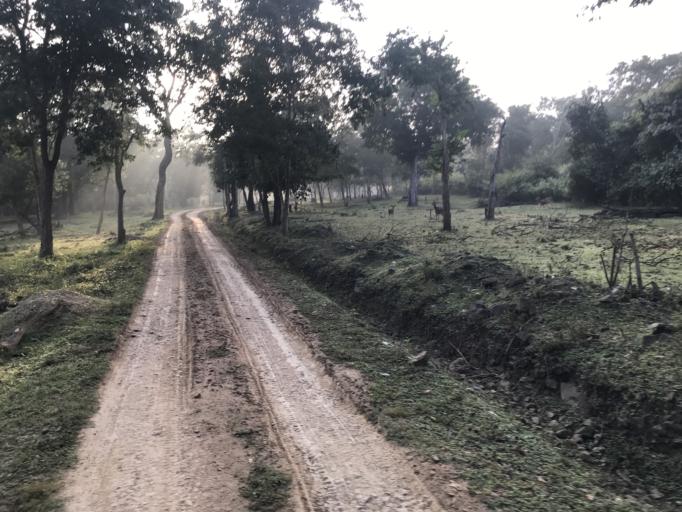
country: IN
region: Karnataka
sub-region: Mysore
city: Heggadadevankote
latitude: 12.0118
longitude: 76.2425
